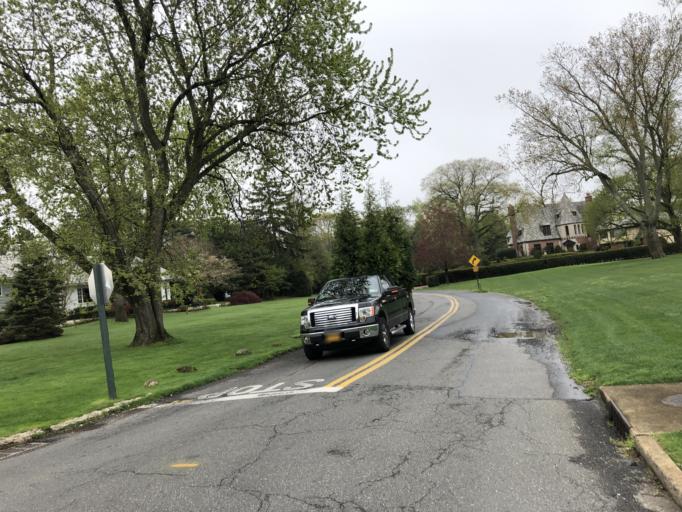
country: US
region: New York
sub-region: Nassau County
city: Hewlett
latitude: 40.6348
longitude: -73.6974
